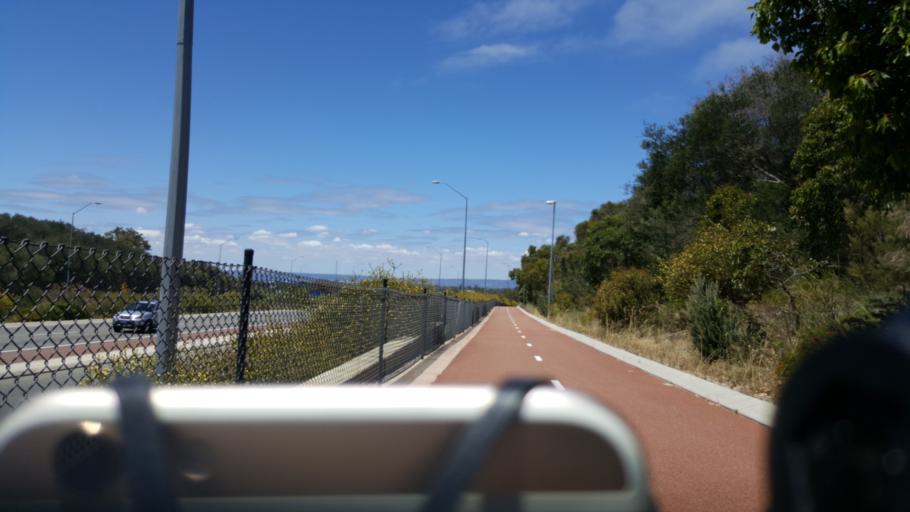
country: AU
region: Western Australia
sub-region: Stirling
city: Westminster
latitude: -31.8676
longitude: 115.8719
